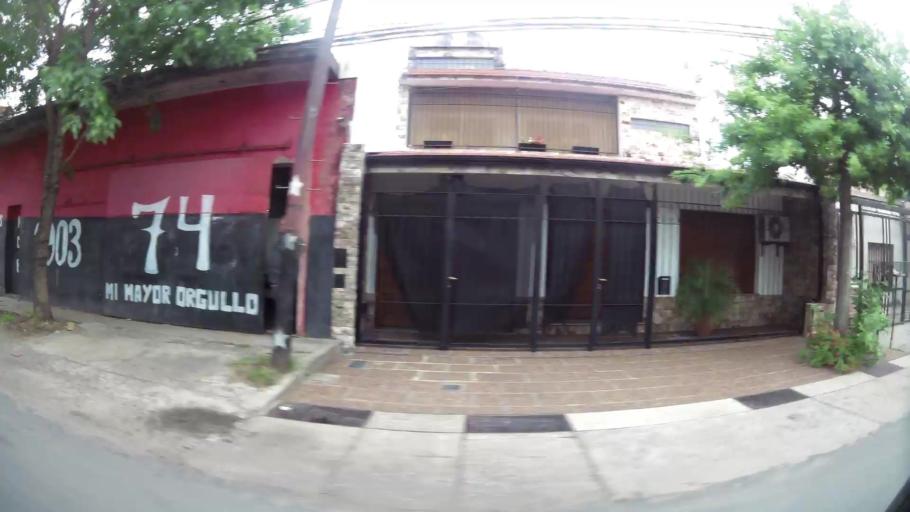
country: AR
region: Santa Fe
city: Gobernador Galvez
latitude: -33.0027
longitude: -60.6605
